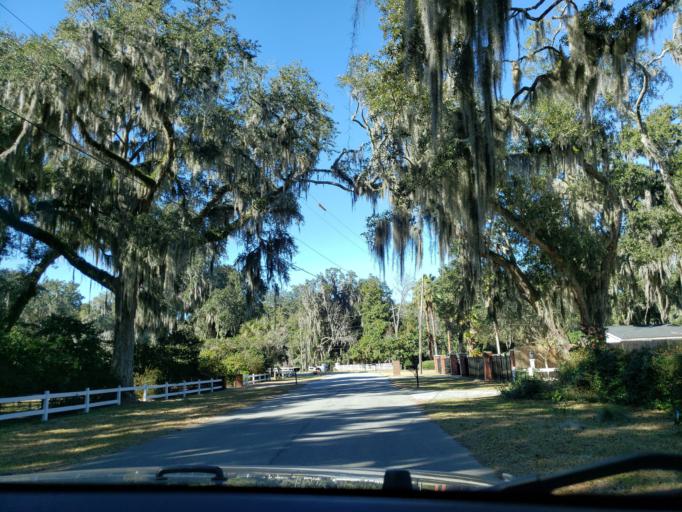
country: US
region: Georgia
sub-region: Chatham County
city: Wilmington Island
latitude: 32.0400
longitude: -80.9708
